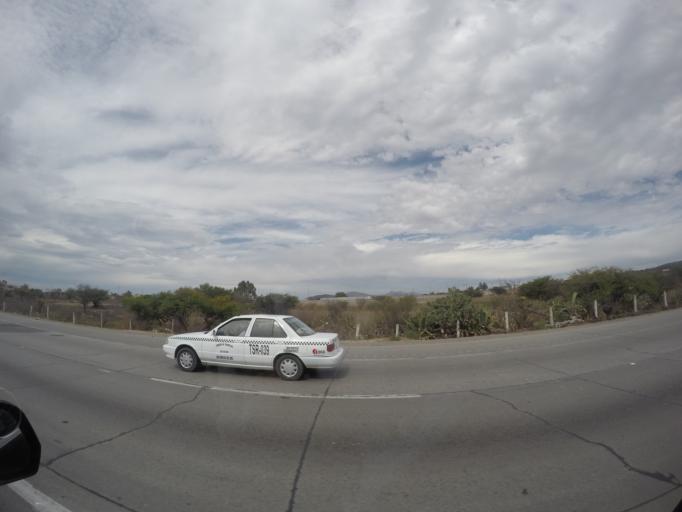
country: MX
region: Queretaro
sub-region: San Juan del Rio
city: Paso de Mata
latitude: 20.3523
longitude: -99.9548
